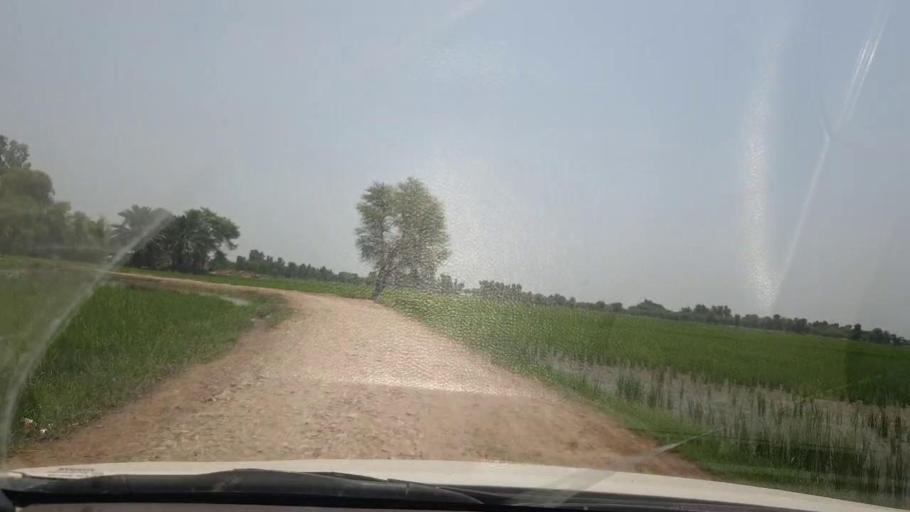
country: PK
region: Sindh
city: Shikarpur
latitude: 27.9190
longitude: 68.6919
